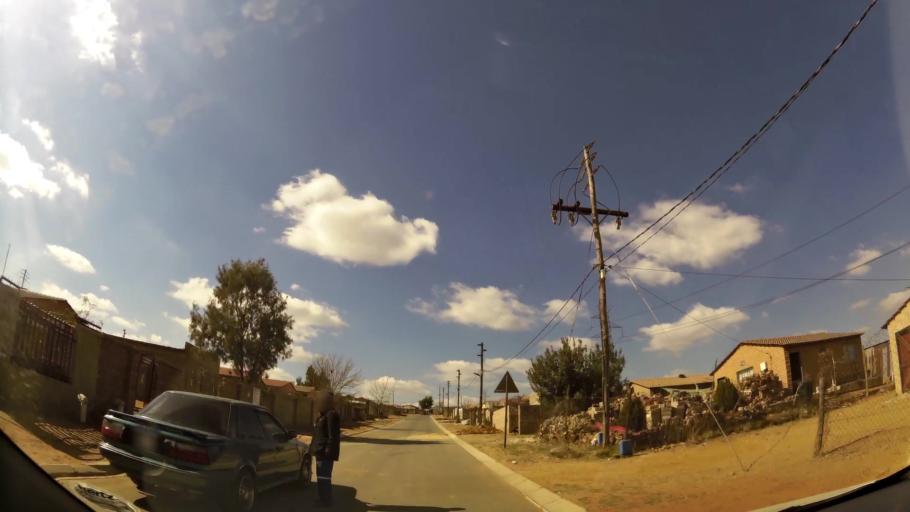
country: ZA
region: Gauteng
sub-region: West Rand District Municipality
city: Krugersdorp
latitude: -26.1380
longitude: 27.7849
